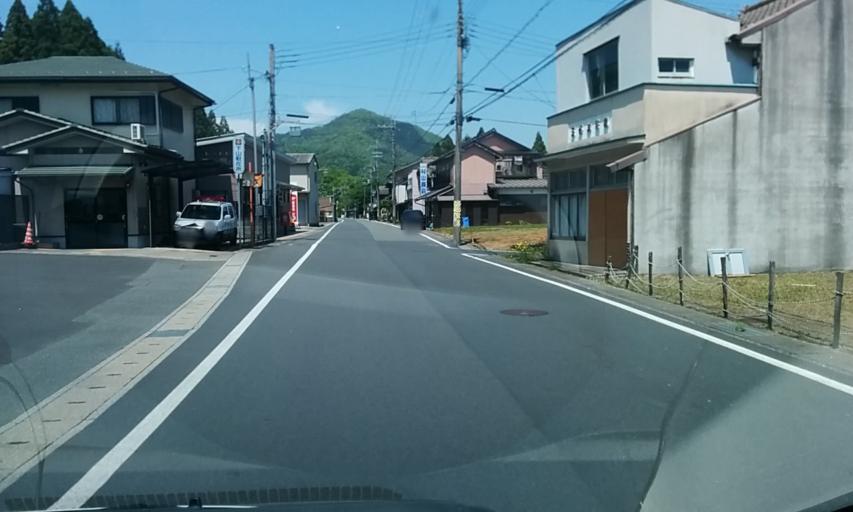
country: JP
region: Kyoto
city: Ayabe
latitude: 35.2125
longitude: 135.4229
